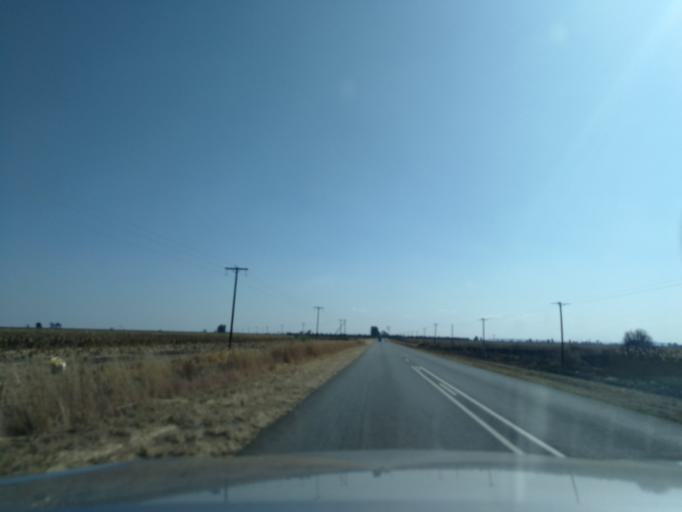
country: ZA
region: North-West
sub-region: Dr Kenneth Kaunda District Municipality
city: Orkney
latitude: -27.0495
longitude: 26.7134
